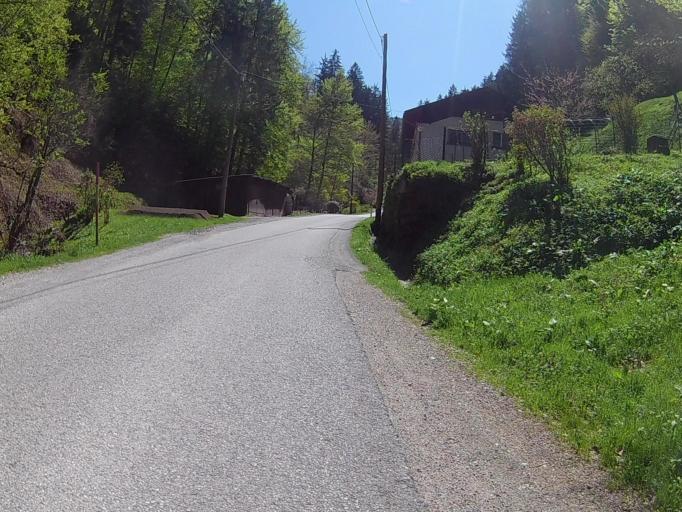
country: SI
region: Ruse
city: Ruse
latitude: 46.5350
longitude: 15.5166
